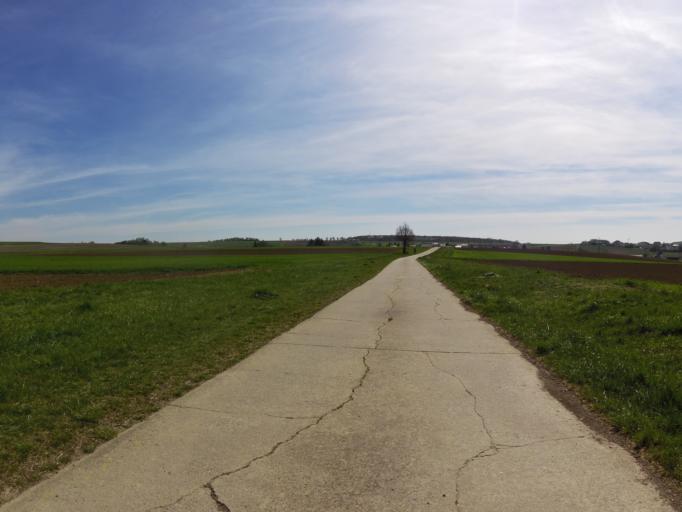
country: DE
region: Bavaria
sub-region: Regierungsbezirk Unterfranken
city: Rimpar
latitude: 49.8543
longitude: 9.9783
